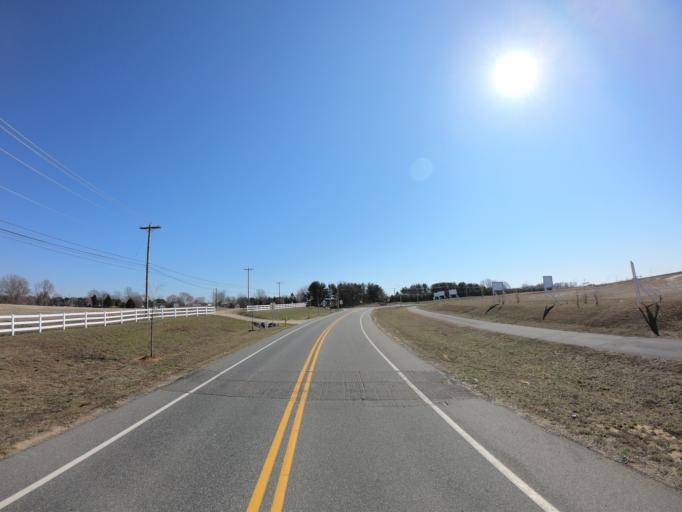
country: US
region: Delaware
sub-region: New Castle County
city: Middletown
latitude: 39.5308
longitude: -75.6796
